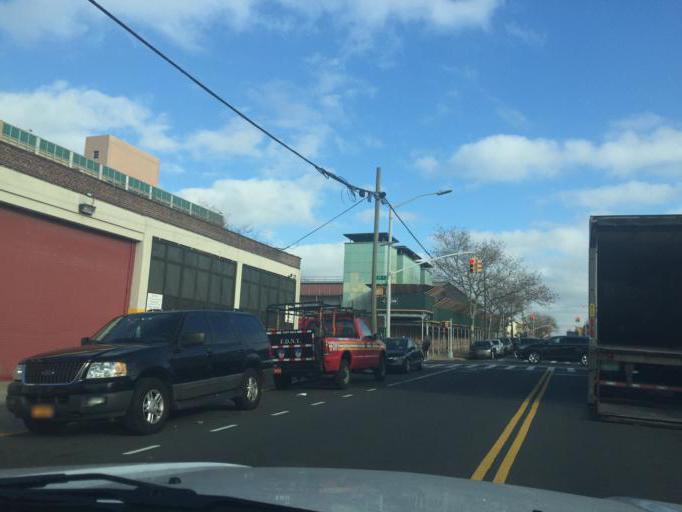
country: US
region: New York
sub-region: Queens County
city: Long Island City
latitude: 40.7425
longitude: -73.9307
